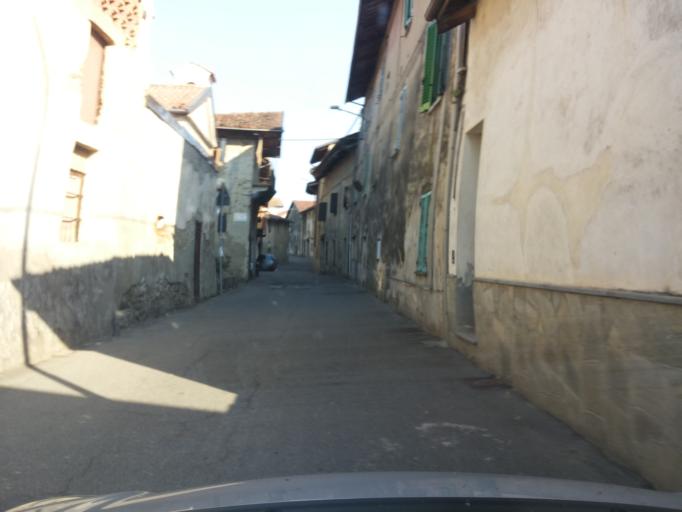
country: IT
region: Piedmont
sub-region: Provincia di Biella
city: Viverone
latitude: 45.4269
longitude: 8.0485
